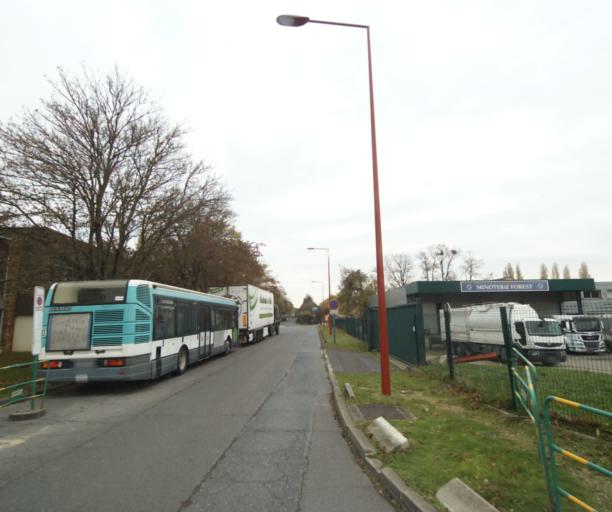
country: FR
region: Ile-de-France
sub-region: Departement du Val-d'Oise
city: Gonesse
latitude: 48.9798
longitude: 2.4602
